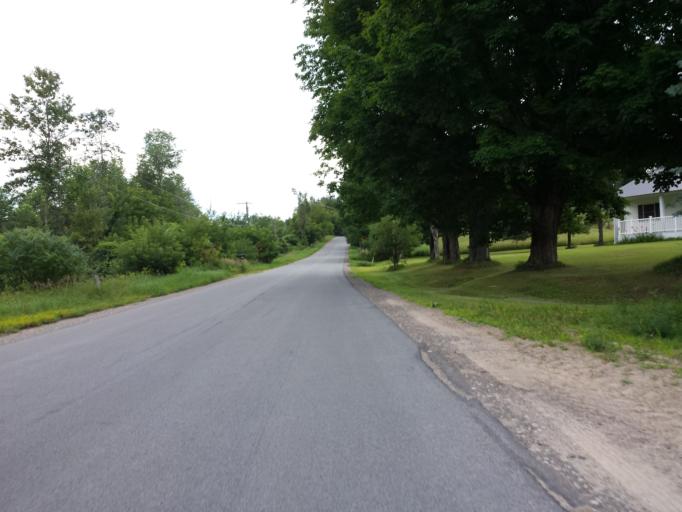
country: US
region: New York
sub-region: St. Lawrence County
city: Norwood
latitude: 44.7222
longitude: -74.9580
